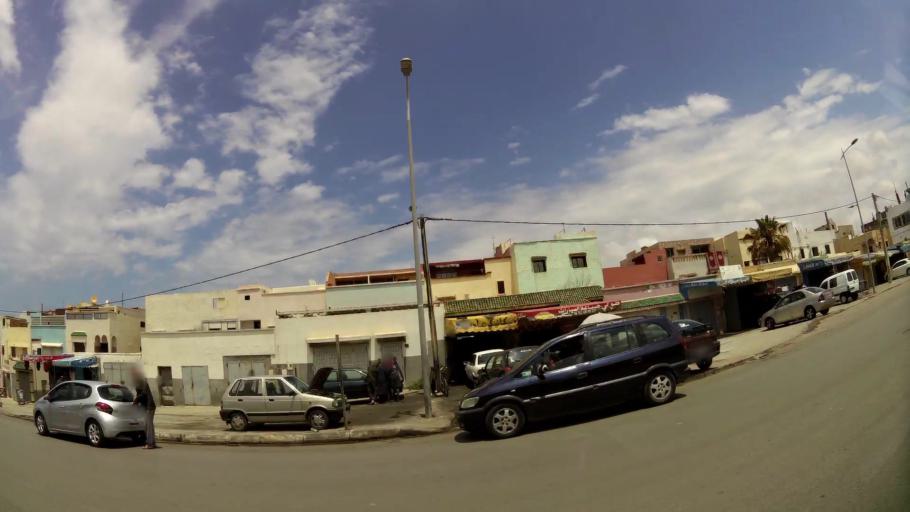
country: MA
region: Rabat-Sale-Zemmour-Zaer
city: Sale
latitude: 34.0461
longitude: -6.8277
